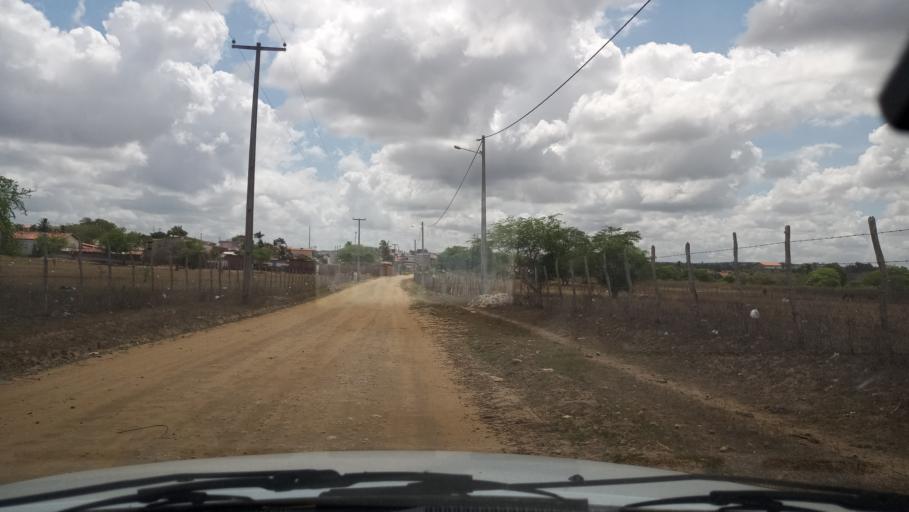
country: BR
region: Rio Grande do Norte
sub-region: Santo Antonio
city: Santo Antonio
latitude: -6.3467
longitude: -35.3792
